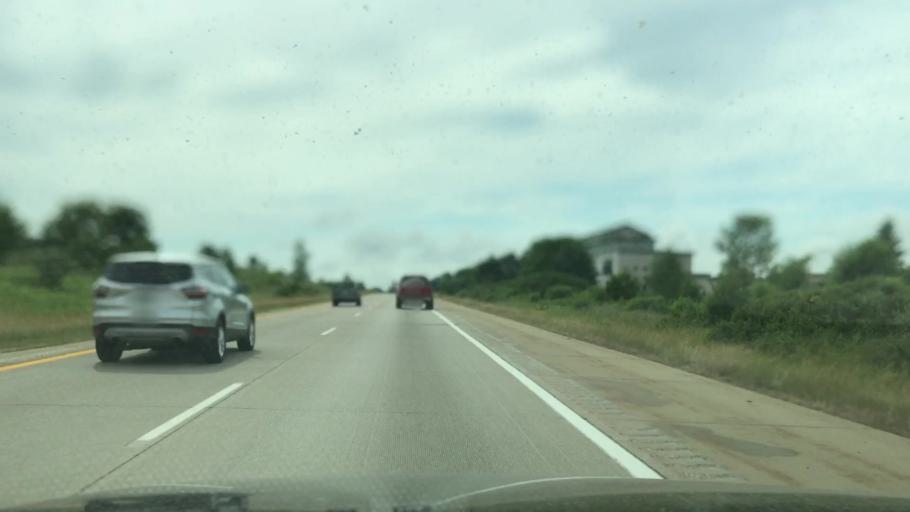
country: US
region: Michigan
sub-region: Kent County
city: Walker
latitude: 43.0179
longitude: -85.7431
